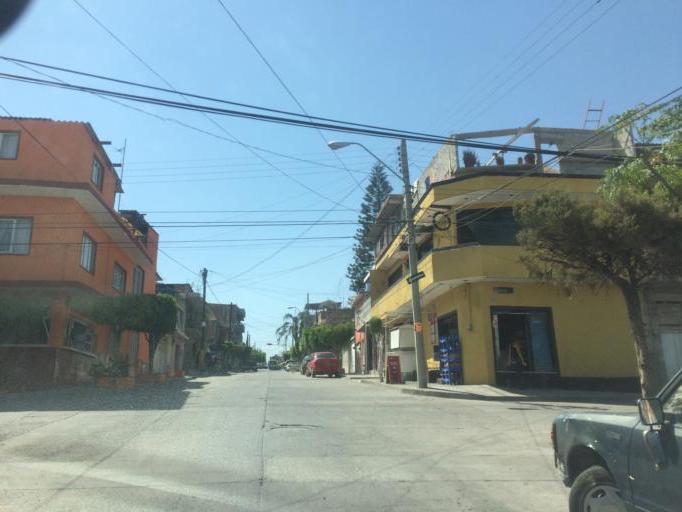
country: MX
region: Guanajuato
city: Leon
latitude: 21.1345
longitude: -101.7015
